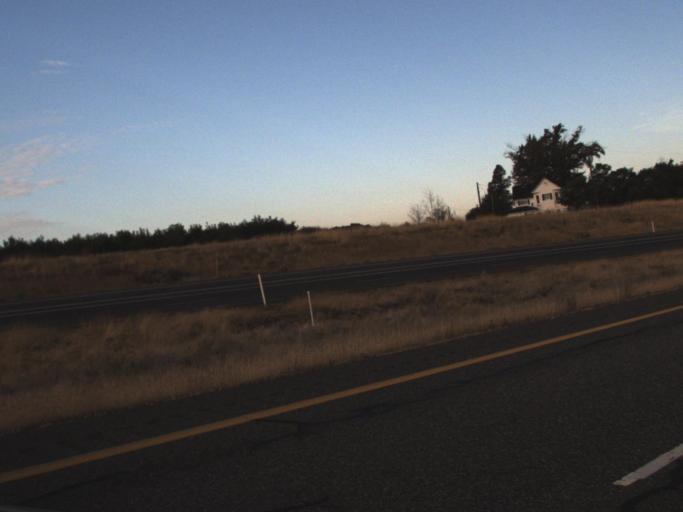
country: US
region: Washington
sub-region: Benton County
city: Prosser
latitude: 46.2112
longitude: -119.7354
